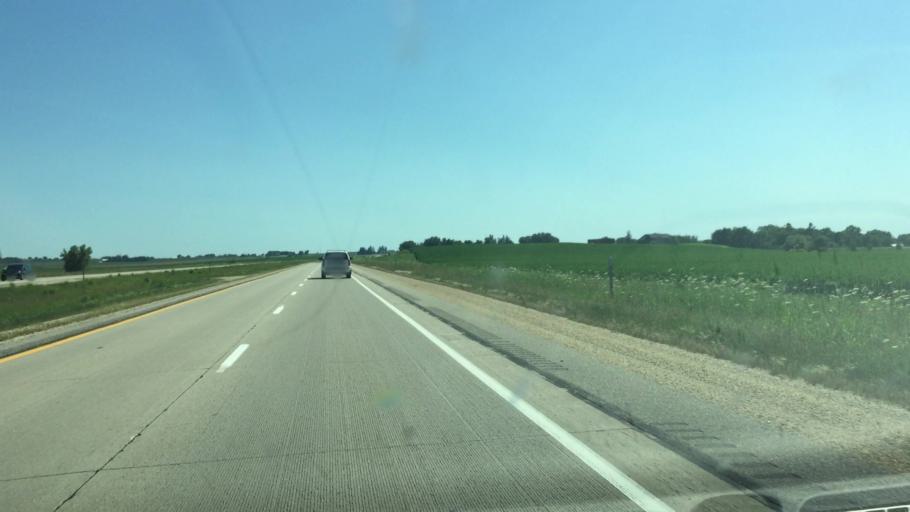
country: US
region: Iowa
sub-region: Jones County
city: Monticello
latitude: 42.1936
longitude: -91.2154
